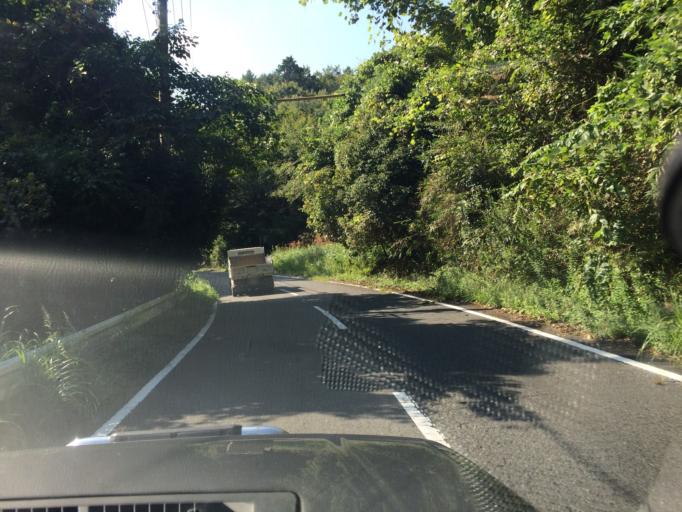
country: JP
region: Mie
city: Nabari
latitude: 34.7033
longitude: 135.9772
